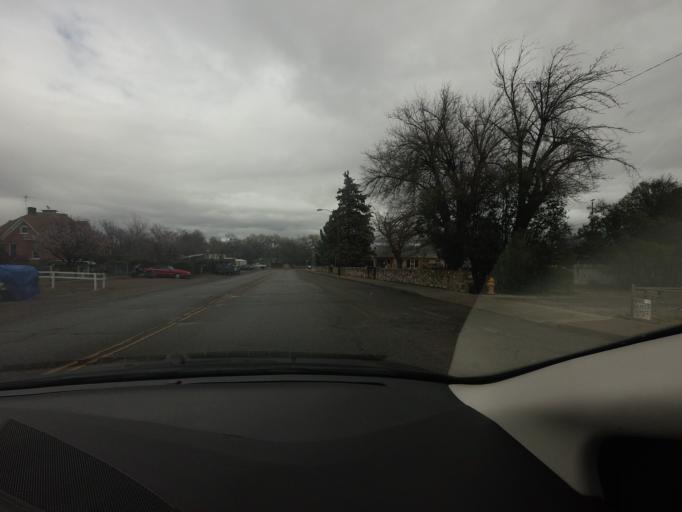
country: US
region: Arizona
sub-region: Yavapai County
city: Cottonwood
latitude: 34.7500
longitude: -112.0291
